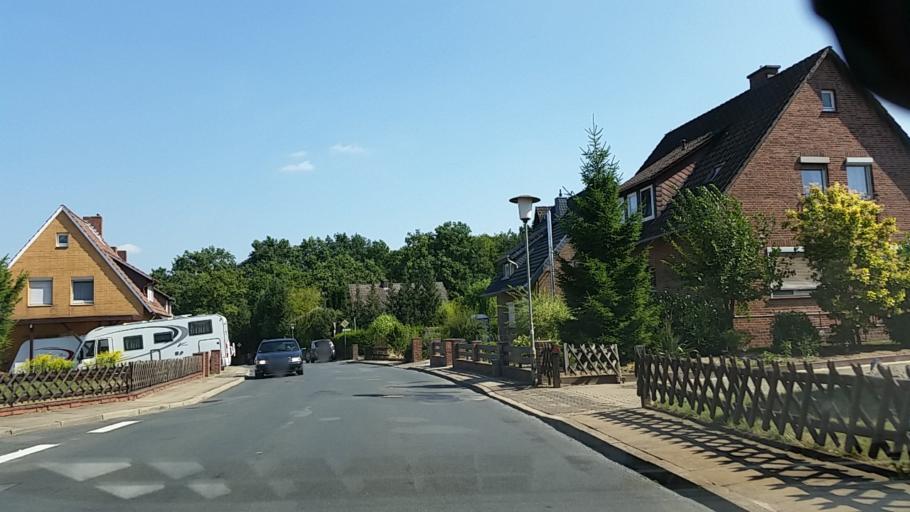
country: DE
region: Lower Saxony
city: Bad Bevensen
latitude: 53.0936
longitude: 10.5614
